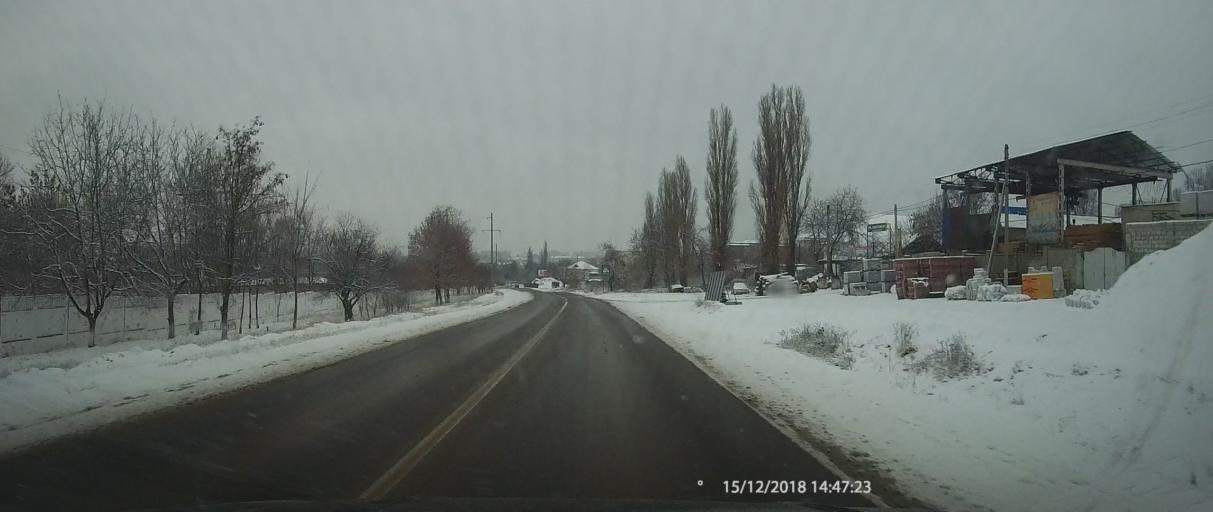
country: MD
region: Cahul
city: Cahul
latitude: 45.8930
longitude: 28.2068
